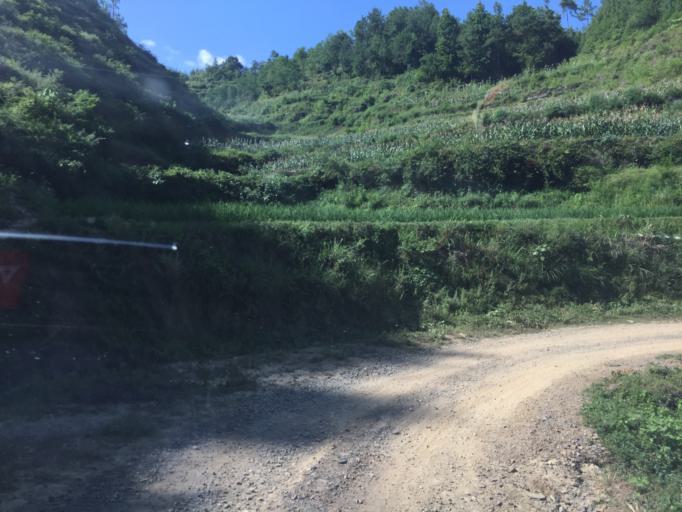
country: CN
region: Guizhou Sheng
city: Jiashi
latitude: 28.3321
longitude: 108.2986
